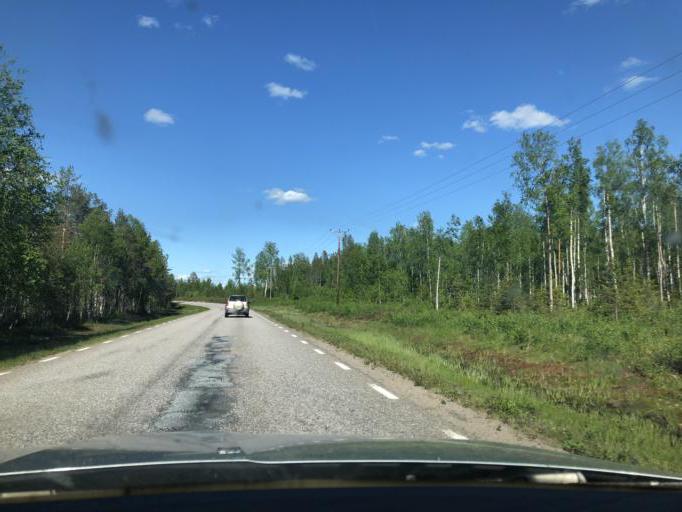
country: SE
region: Norrbotten
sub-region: Kalix Kommun
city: Kalix
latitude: 66.0243
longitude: 23.1595
